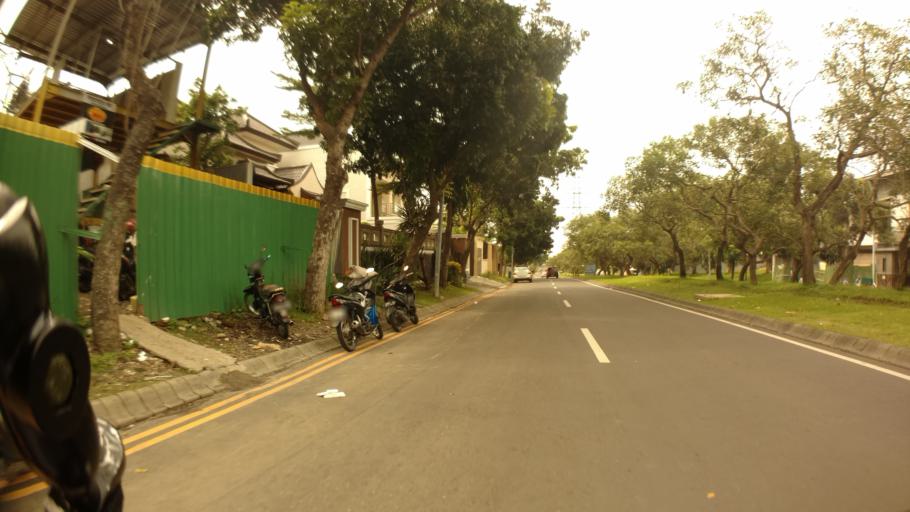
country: ID
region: East Java
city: Driyorejo
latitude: -7.2901
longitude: 112.6479
